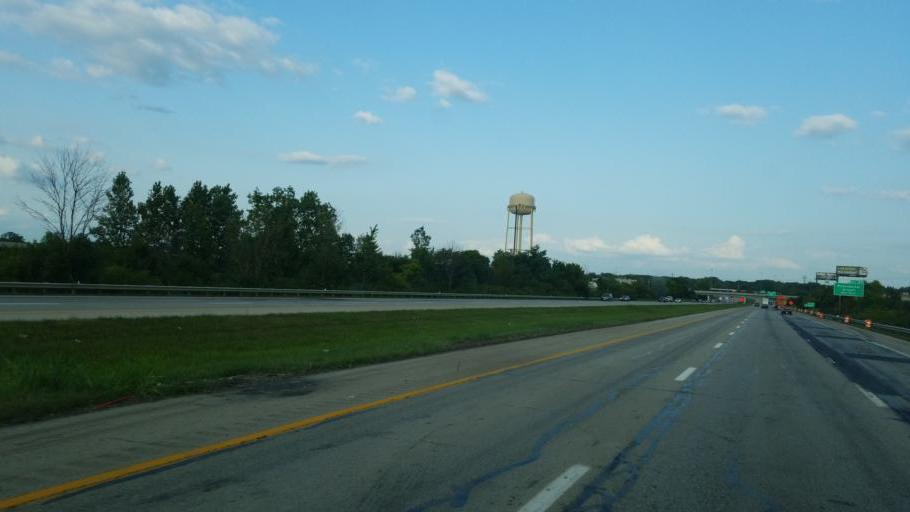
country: US
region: Ohio
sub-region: Franklin County
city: Obetz
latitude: 39.8716
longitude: -82.9489
